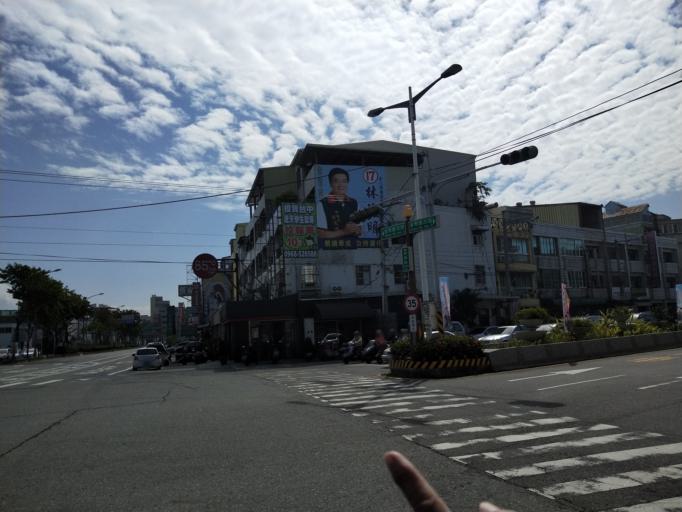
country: TW
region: Taiwan
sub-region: Changhua
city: Chang-hua
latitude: 24.0763
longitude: 120.5305
